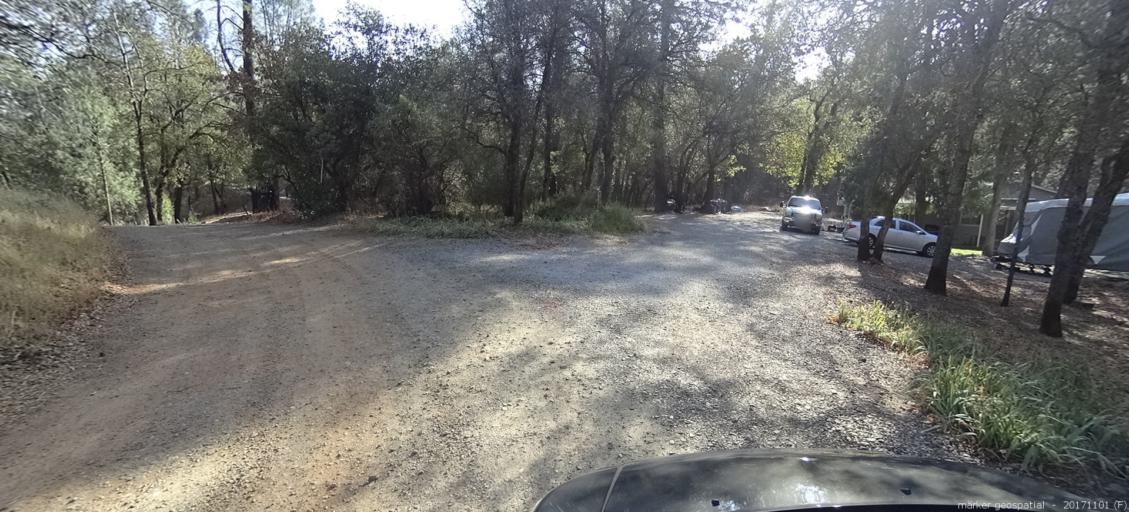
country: US
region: California
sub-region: Shasta County
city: Shasta Lake
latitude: 40.7074
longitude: -122.3199
